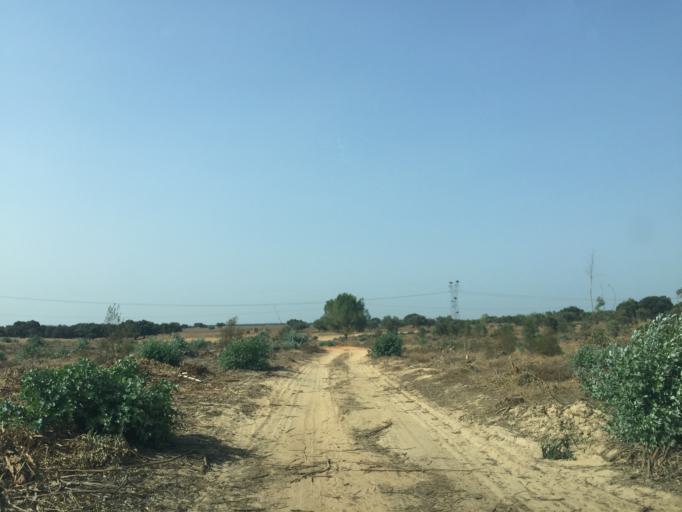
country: PT
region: Beja
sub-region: Aljustrel
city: Aljustrel
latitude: 38.0247
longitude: -8.3588
